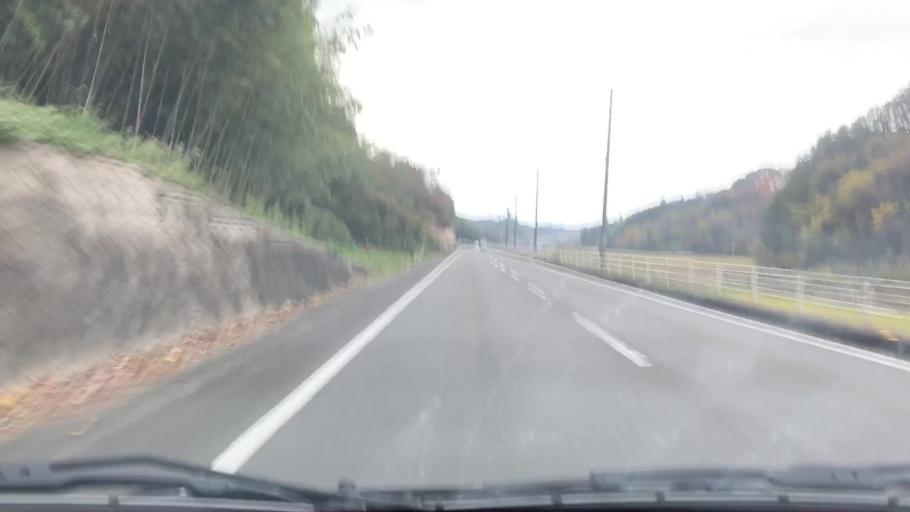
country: JP
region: Saga Prefecture
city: Ureshinomachi-shimojuku
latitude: 33.1181
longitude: 129.9776
